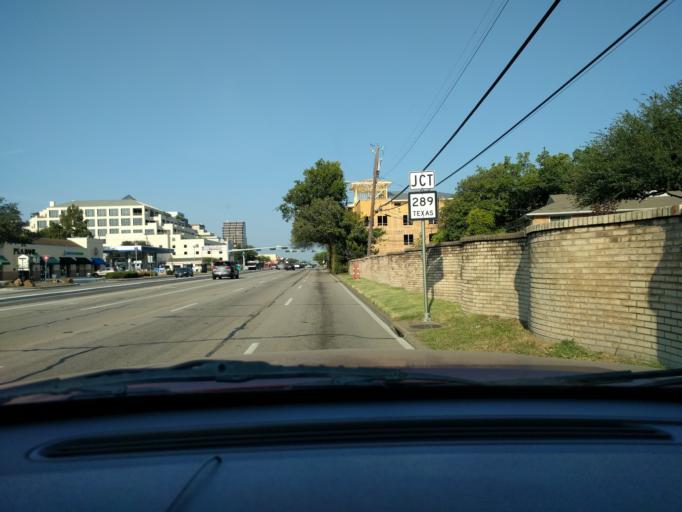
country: US
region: Texas
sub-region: Dallas County
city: University Park
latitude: 32.8657
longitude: -96.8024
